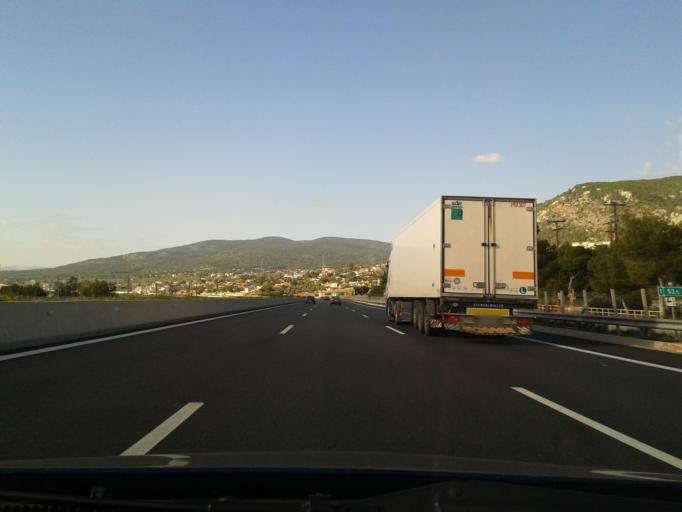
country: GR
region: Attica
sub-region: Nomarchia Dytikis Attikis
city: Kineta
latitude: 37.9741
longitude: 23.2223
